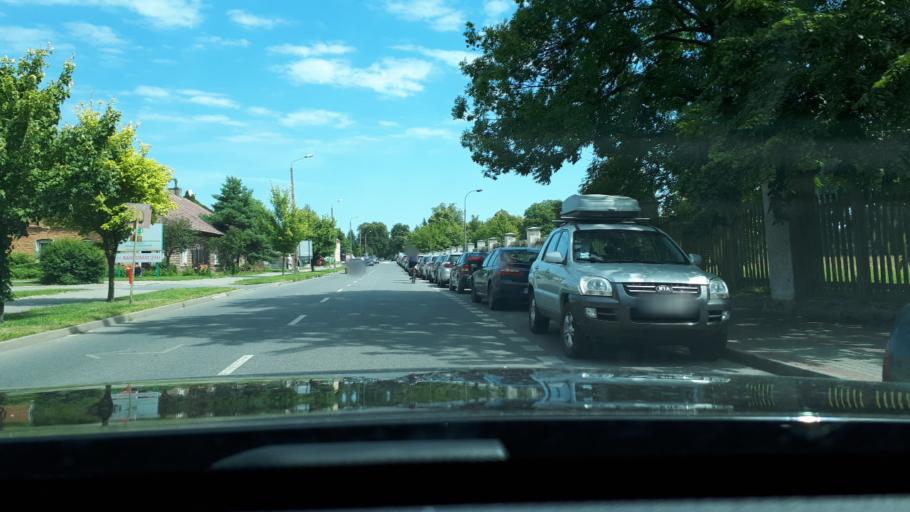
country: PL
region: Lodz Voivodeship
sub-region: powiat Lowicki
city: Nieborow
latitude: 52.0689
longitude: 20.0706
